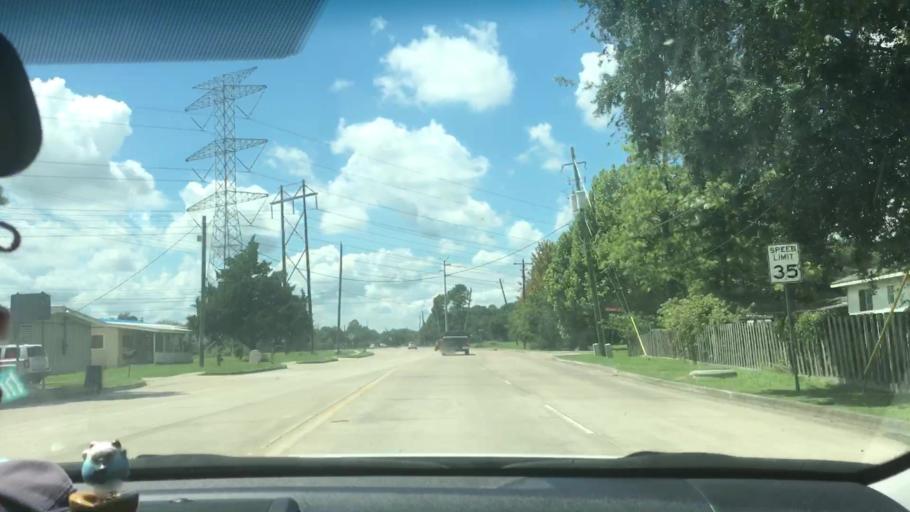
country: US
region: Texas
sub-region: Fort Bend County
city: Missouri City
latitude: 29.6101
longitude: -95.5435
